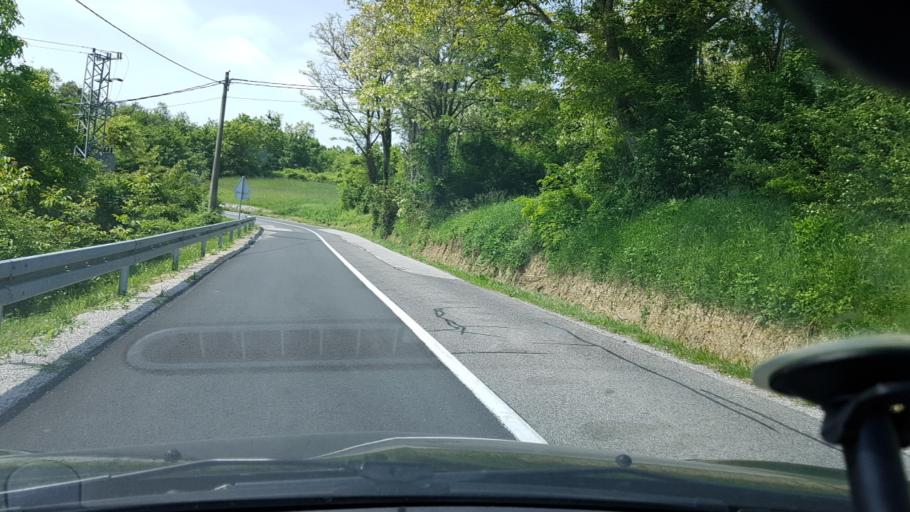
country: HR
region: Krapinsko-Zagorska
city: Marija Bistrica
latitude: 46.0080
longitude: 16.0915
